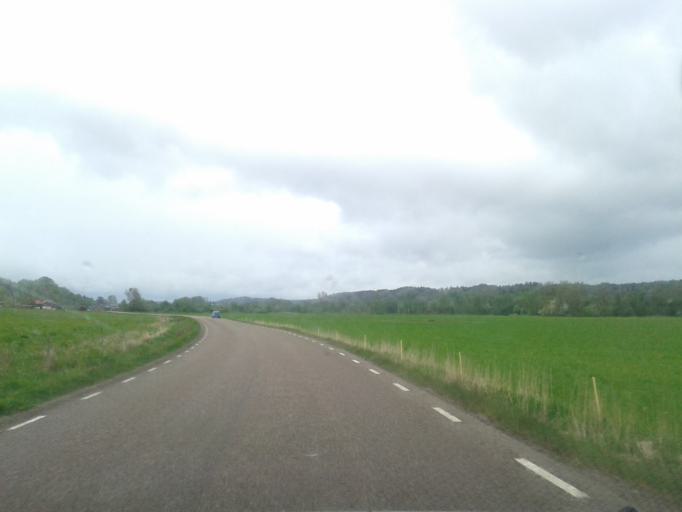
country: SE
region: Vaestra Goetaland
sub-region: Lilla Edets Kommun
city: Lodose
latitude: 58.0253
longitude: 12.1378
